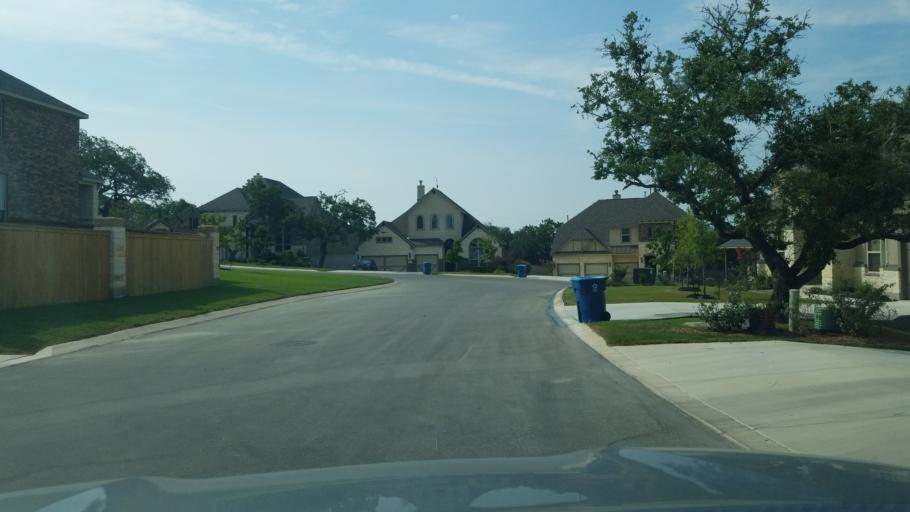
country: US
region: Texas
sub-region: Bexar County
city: Scenic Oaks
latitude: 29.7248
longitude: -98.6600
